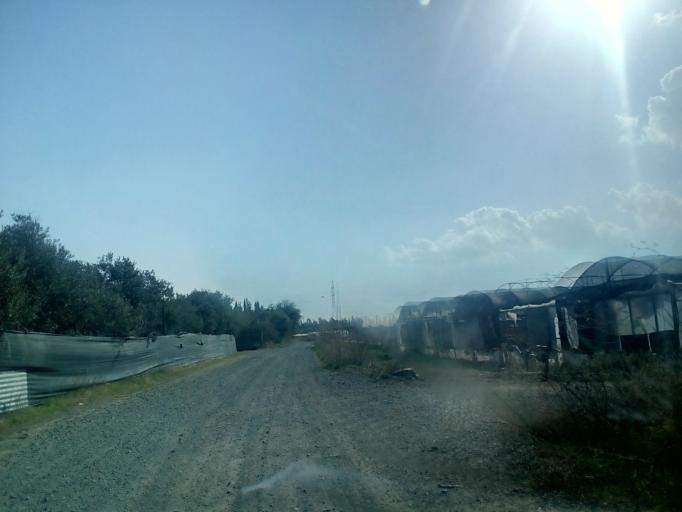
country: CY
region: Limassol
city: Ypsonas
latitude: 34.6716
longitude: 32.9694
